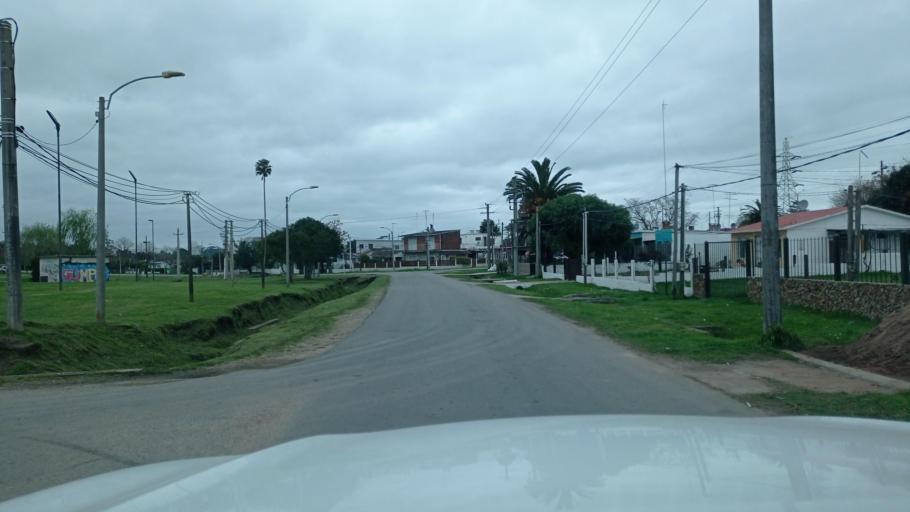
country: UY
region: Canelones
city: Toledo
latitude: -34.7783
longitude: -56.1357
